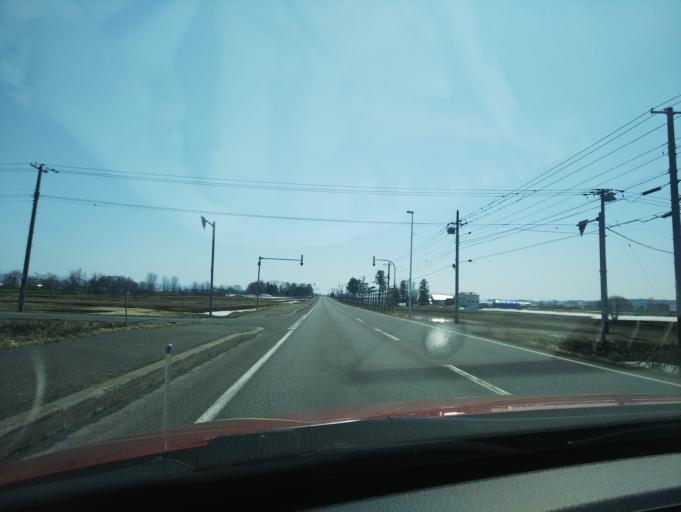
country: JP
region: Hokkaido
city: Nayoro
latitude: 44.2261
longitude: 142.3948
